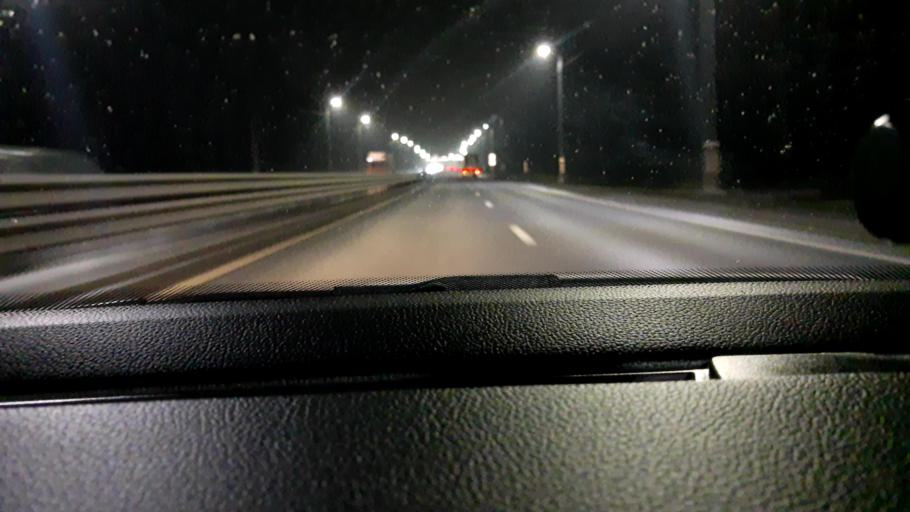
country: RU
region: Moskovskaya
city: Malaya Dubna
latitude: 55.8649
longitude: 38.9129
